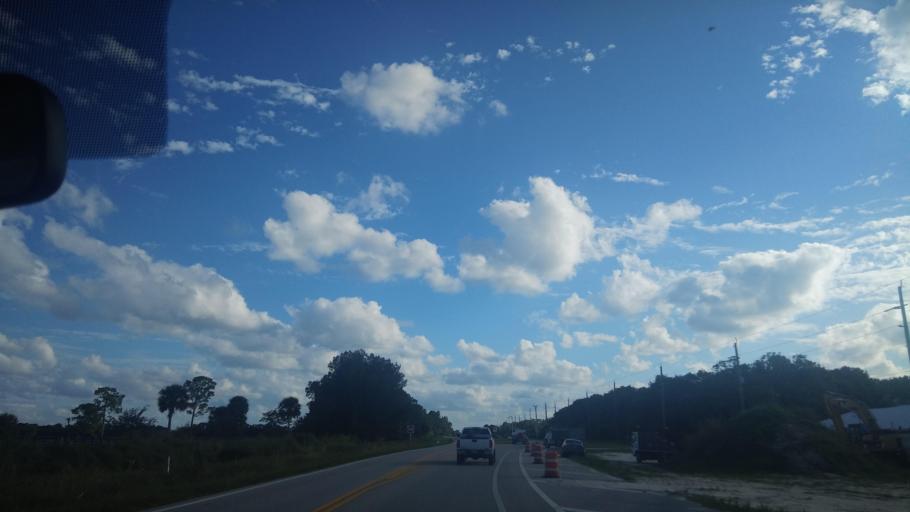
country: US
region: Florida
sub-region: Indian River County
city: Winter Beach
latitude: 27.6876
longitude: -80.4629
